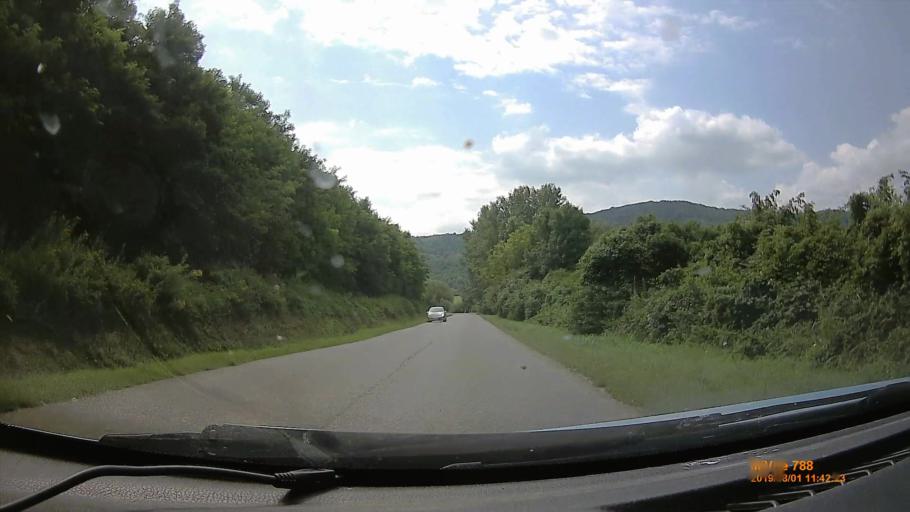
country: HU
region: Baranya
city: Villany
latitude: 45.8855
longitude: 18.4114
